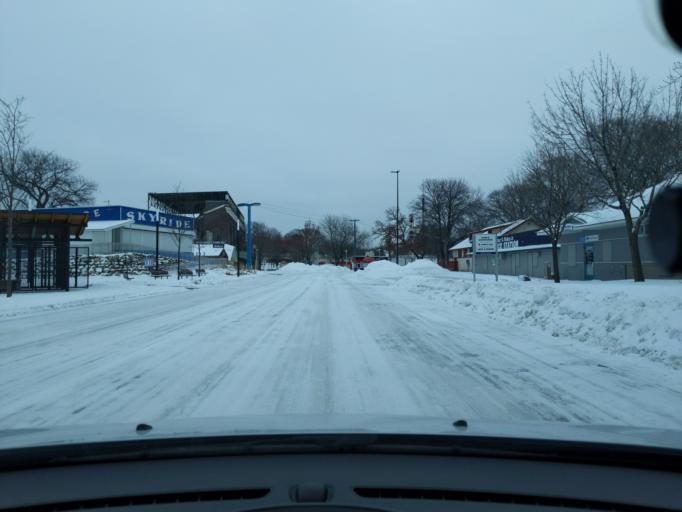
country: US
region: Minnesota
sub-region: Ramsey County
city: Falcon Heights
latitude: 44.9807
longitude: -93.1767
